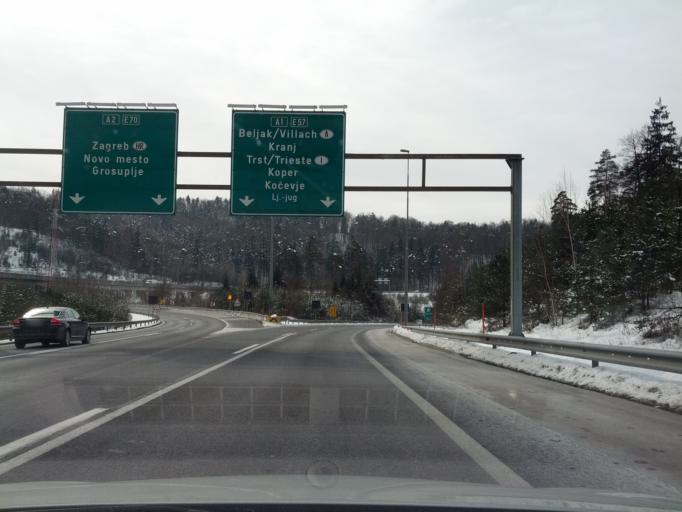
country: SI
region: Skofljica
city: Lavrica
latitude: 46.0161
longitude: 14.5574
